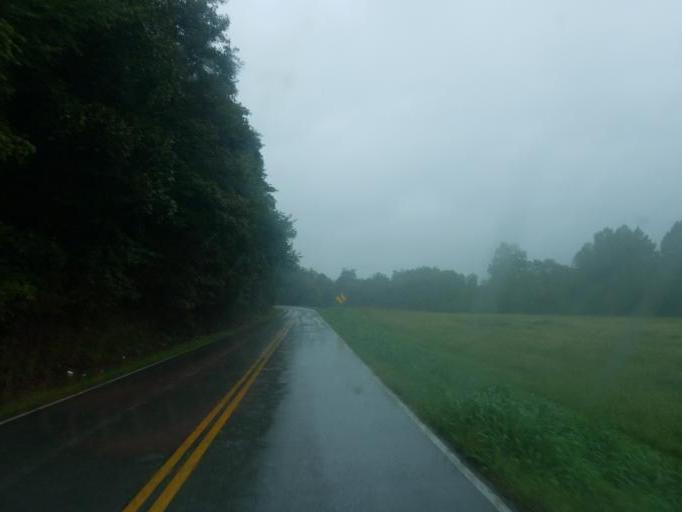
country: US
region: Kentucky
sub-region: Carter County
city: Grayson
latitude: 38.4635
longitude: -83.0533
